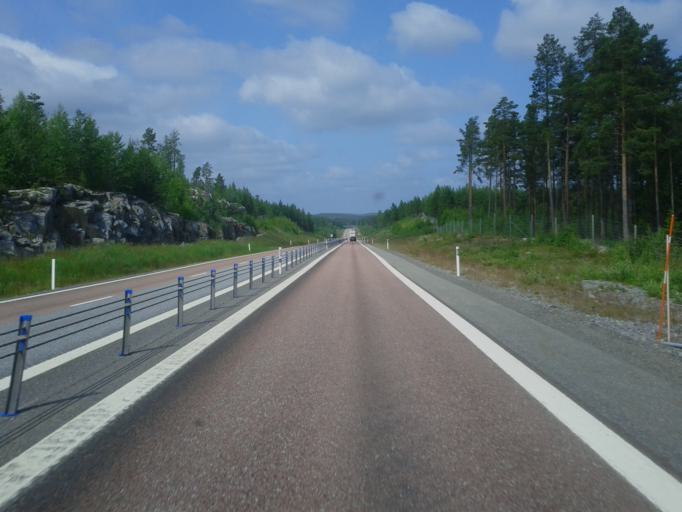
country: SE
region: Vaesterbotten
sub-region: Skelleftea Kommun
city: Soedra Bergsbyn
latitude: 64.6898
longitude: 21.0430
